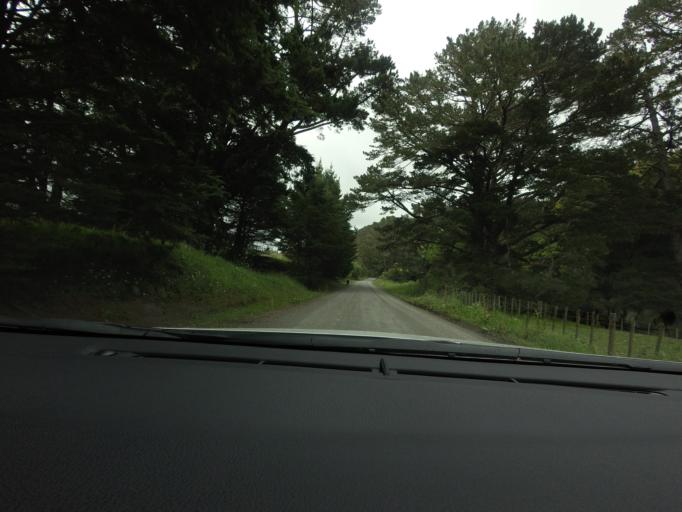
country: NZ
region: Auckland
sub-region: Auckland
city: Warkworth
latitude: -36.4757
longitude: 174.5669
